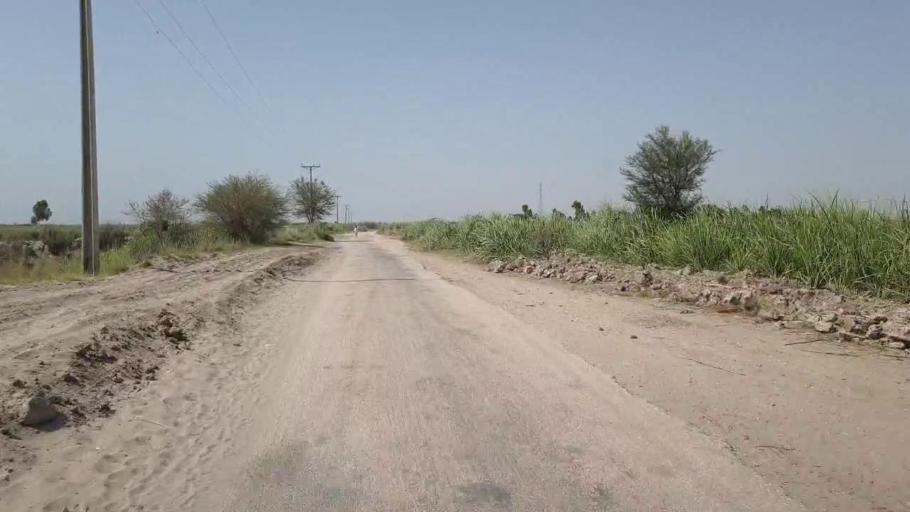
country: PK
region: Sindh
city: Jam Sahib
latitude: 26.4226
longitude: 68.9077
